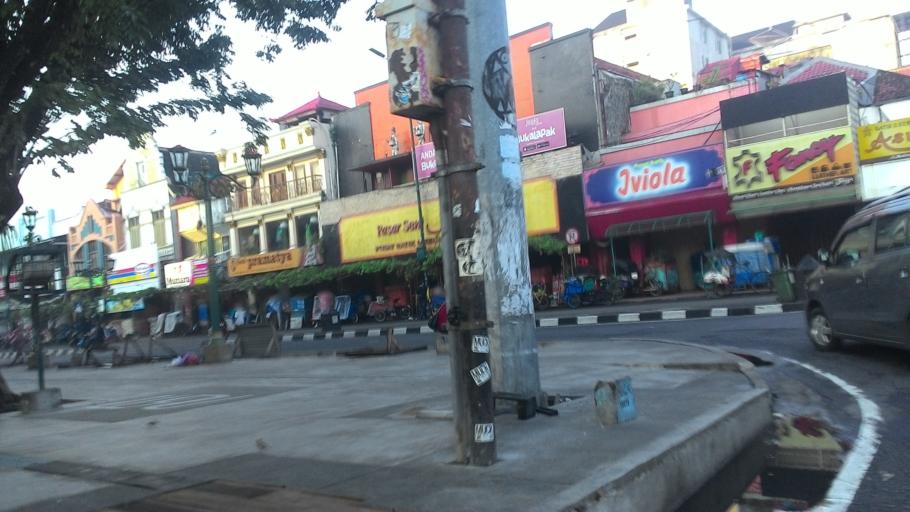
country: ID
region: Daerah Istimewa Yogyakarta
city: Yogyakarta
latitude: -7.7901
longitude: 110.3663
